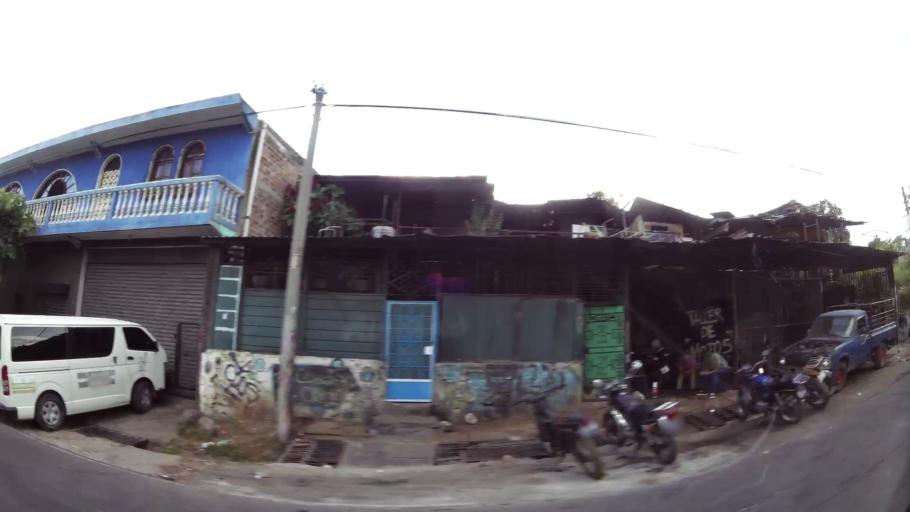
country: SV
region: Cuscatlan
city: Cojutepeque
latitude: 13.7149
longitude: -88.9319
